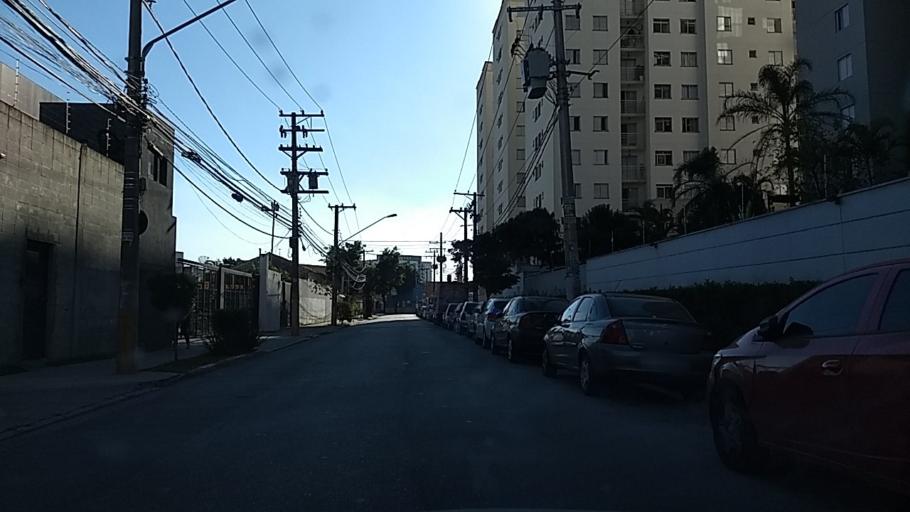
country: BR
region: Sao Paulo
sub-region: Sao Paulo
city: Sao Paulo
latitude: -23.5192
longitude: -46.6028
